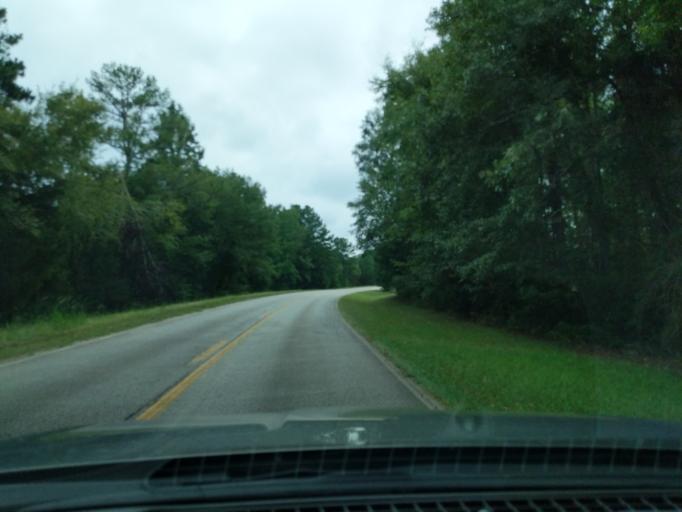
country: US
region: Georgia
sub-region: Columbia County
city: Appling
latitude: 33.5882
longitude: -82.3775
